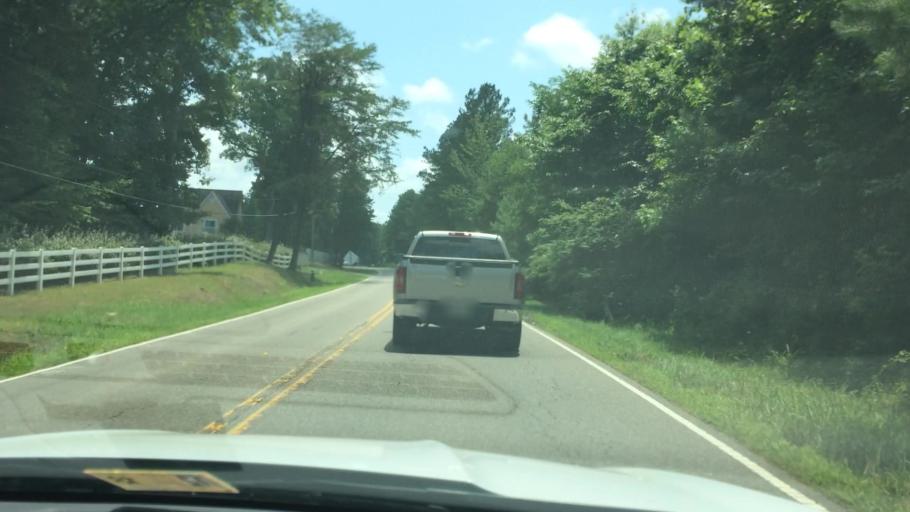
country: US
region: Virginia
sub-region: City of Williamsburg
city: Williamsburg
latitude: 37.2710
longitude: -76.6388
